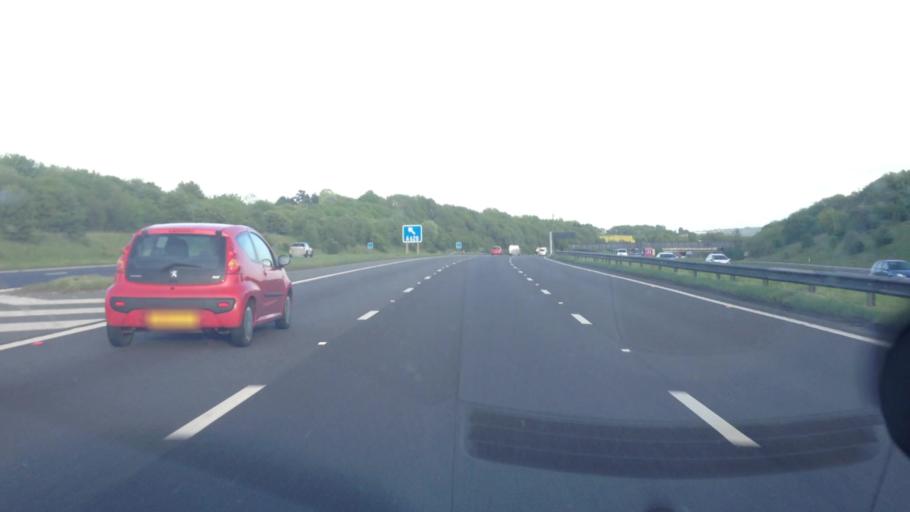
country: GB
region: England
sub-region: Barnsley
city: Dodworth
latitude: 53.5527
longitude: -1.5212
